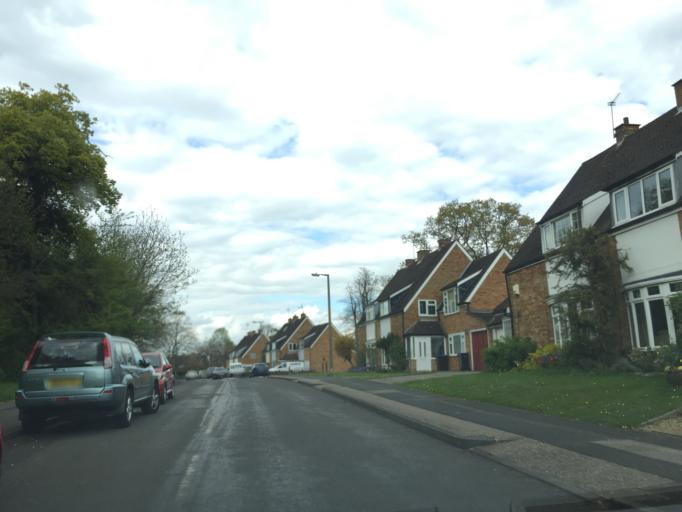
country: GB
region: England
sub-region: Essex
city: Harlow
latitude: 51.7713
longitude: 0.0802
